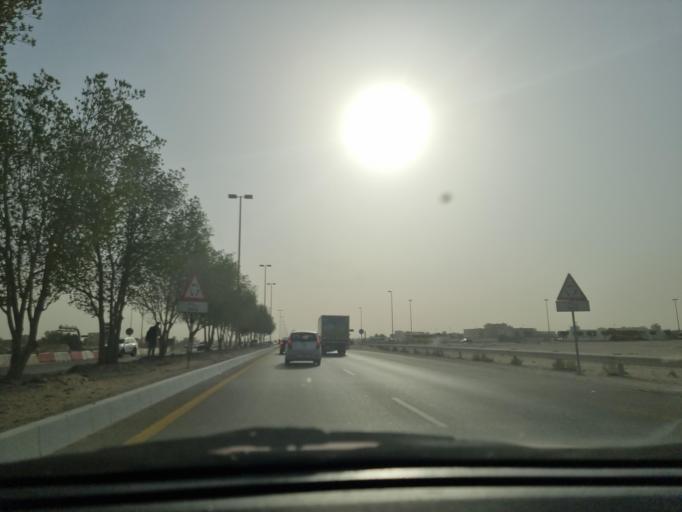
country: AE
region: Abu Dhabi
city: Abu Dhabi
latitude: 24.4008
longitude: 54.7152
